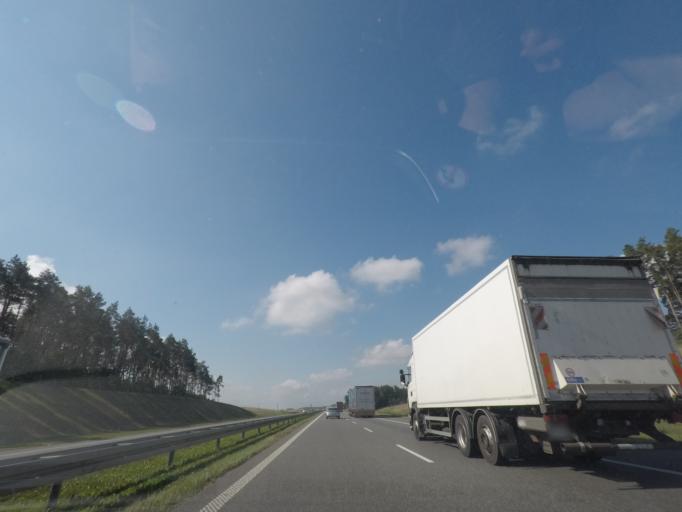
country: PL
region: Pomeranian Voivodeship
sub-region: Powiat tczewski
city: Pelplin
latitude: 53.9007
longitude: 18.6401
